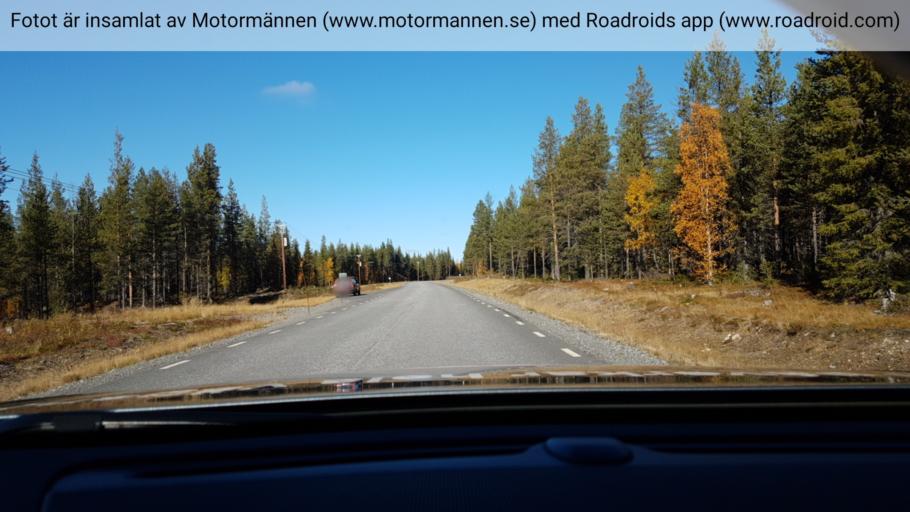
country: SE
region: Norrbotten
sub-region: Gallivare Kommun
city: Gaellivare
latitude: 66.8244
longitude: 21.0414
